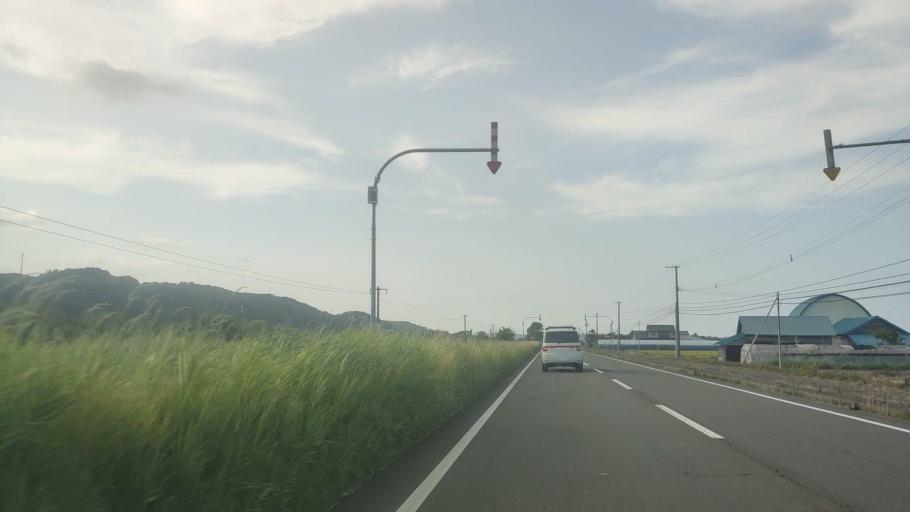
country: JP
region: Hokkaido
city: Iwamizawa
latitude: 42.9923
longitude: 141.7907
